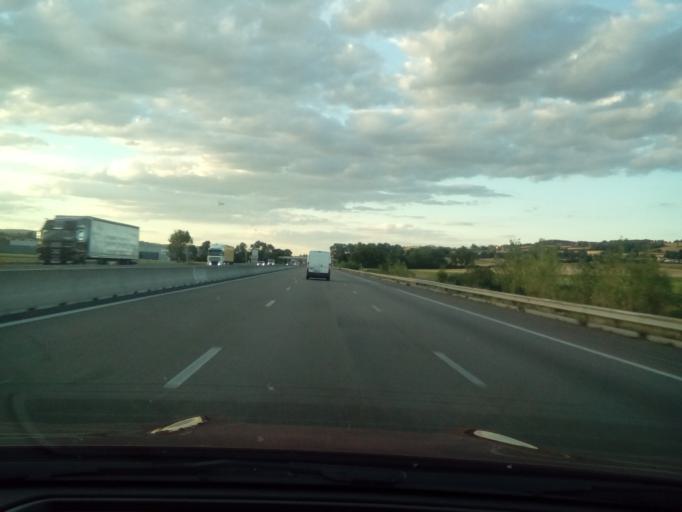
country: FR
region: Rhone-Alpes
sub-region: Departement de l'Isere
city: Reventin-Vaugris
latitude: 45.4539
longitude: 4.8302
